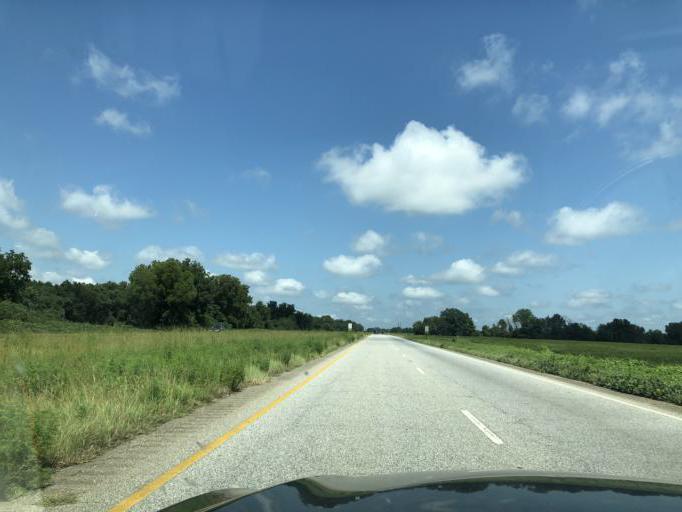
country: US
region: Alabama
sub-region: Henry County
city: Abbeville
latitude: 31.5983
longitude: -85.2770
